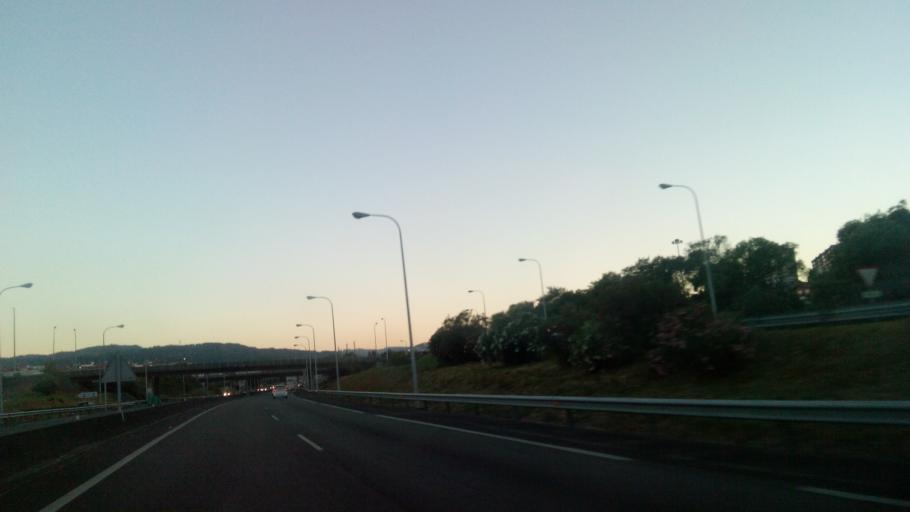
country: ES
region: Galicia
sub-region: Provincia de Pontevedra
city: Pontevedra
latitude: 42.4403
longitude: -8.6489
